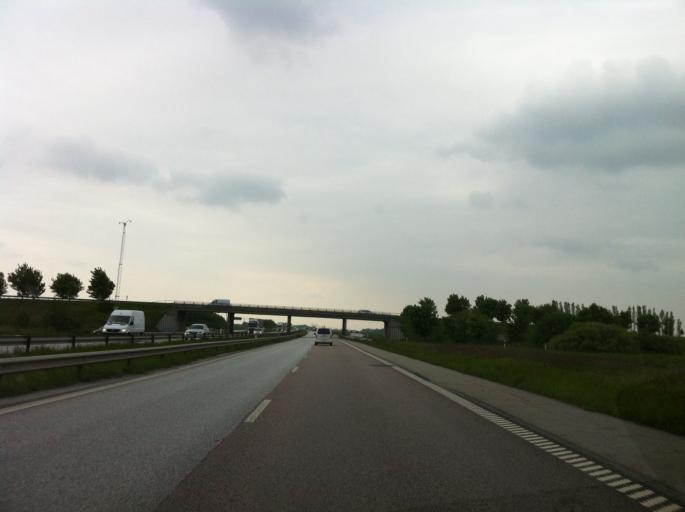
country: SE
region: Skane
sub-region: Lomma Kommun
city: Lomma
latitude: 55.6880
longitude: 13.0975
